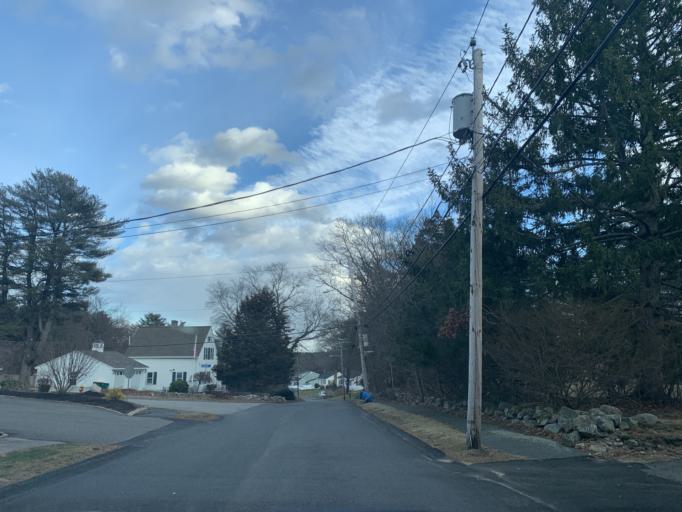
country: US
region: Massachusetts
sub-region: Norfolk County
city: Norwood
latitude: 42.1776
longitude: -71.1788
